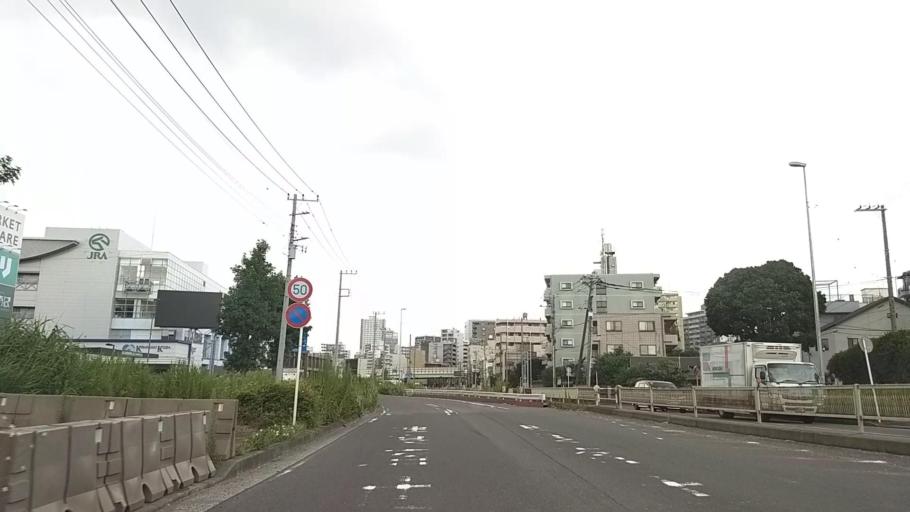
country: JP
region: Kanagawa
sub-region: Kawasaki-shi
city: Kawasaki
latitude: 35.5342
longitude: 139.7119
